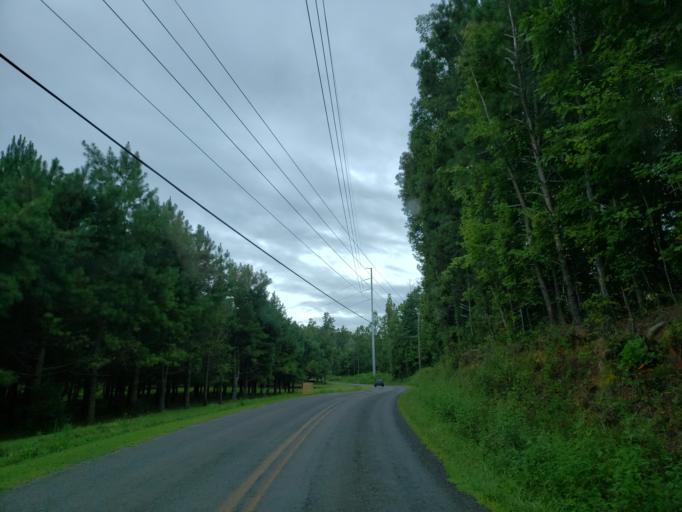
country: US
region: Georgia
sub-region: Gilmer County
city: Ellijay
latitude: 34.6090
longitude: -84.5681
